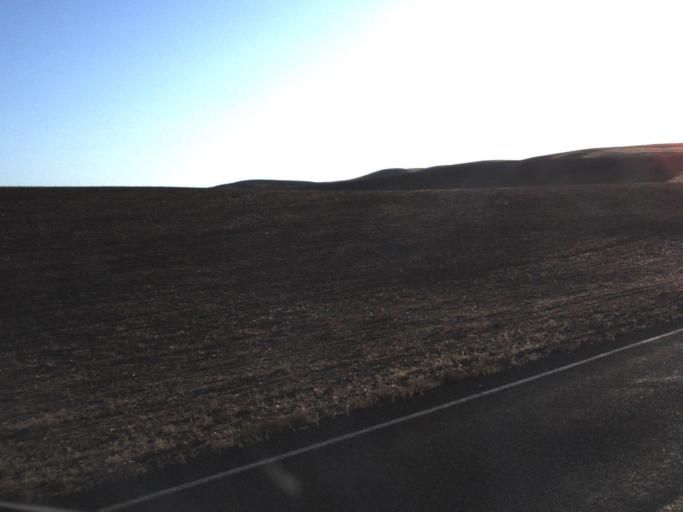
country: US
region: Washington
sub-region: Adams County
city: Ritzville
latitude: 46.6774
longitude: -118.3607
